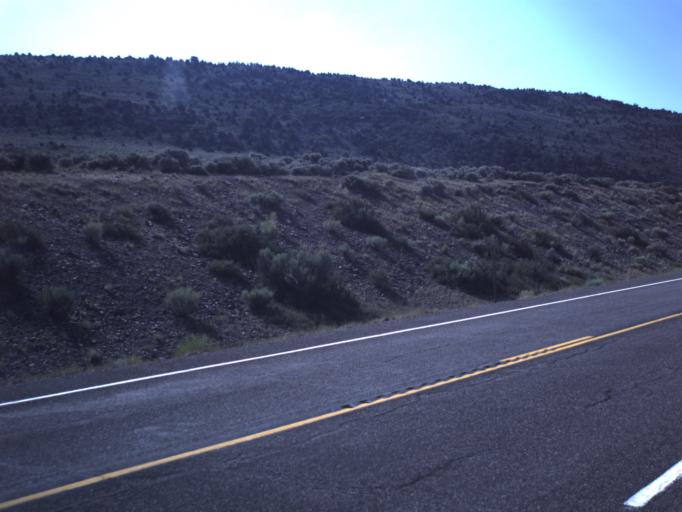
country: US
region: Utah
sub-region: Wayne County
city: Loa
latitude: 38.4957
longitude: -111.8331
